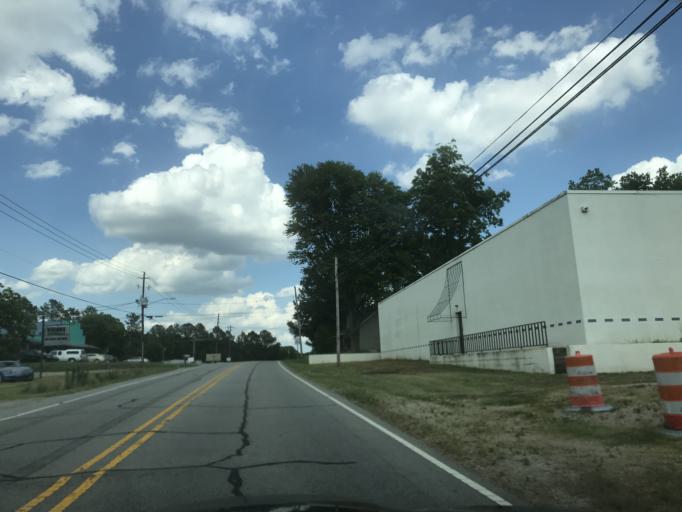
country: US
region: North Carolina
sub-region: Nash County
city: Spring Hope
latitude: 35.9517
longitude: -78.1007
